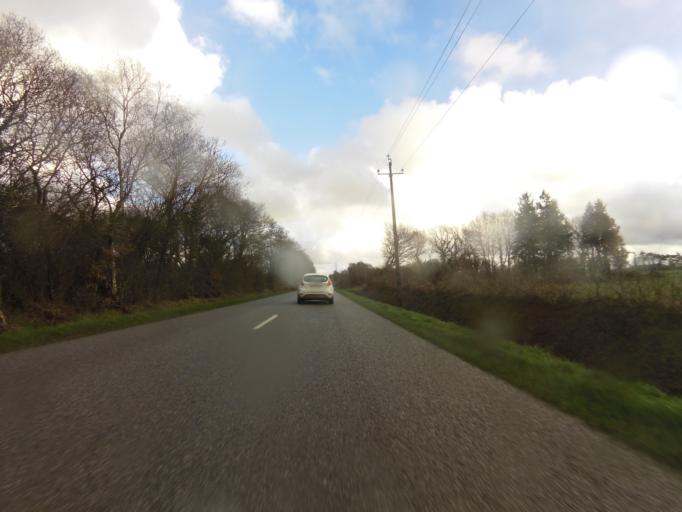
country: FR
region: Brittany
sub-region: Departement du Morbihan
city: Langonnet
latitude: 48.1442
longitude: -3.4837
